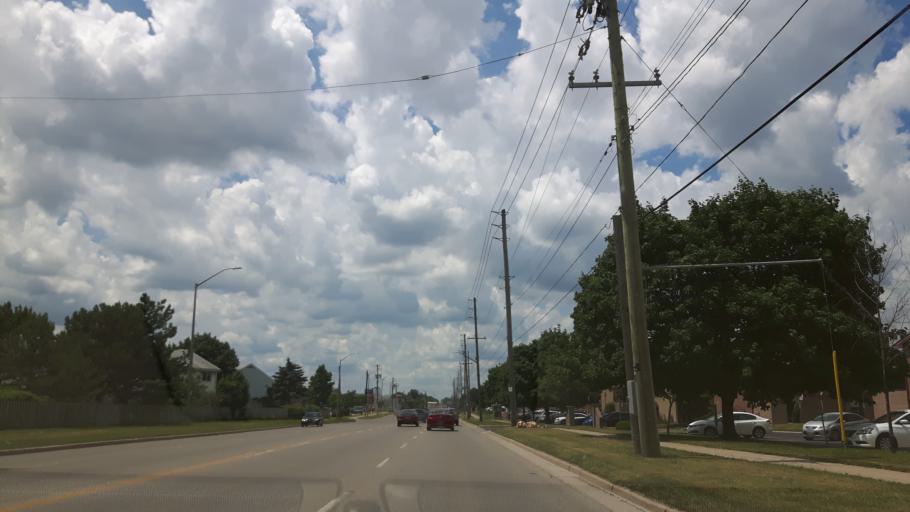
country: CA
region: Ontario
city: London
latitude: 42.9424
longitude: -81.2392
